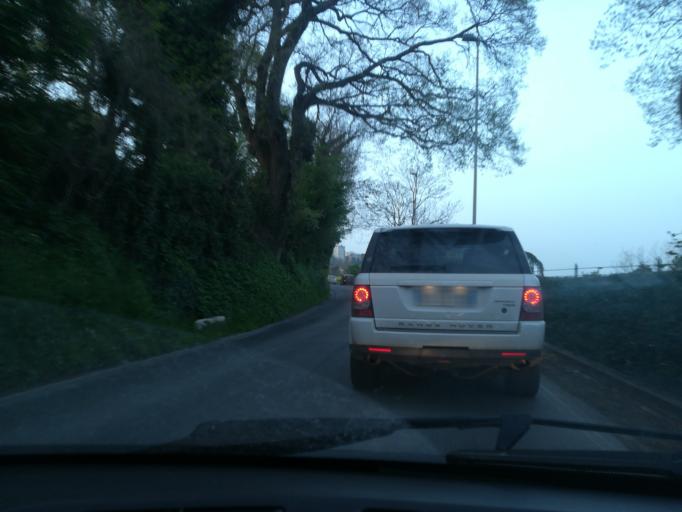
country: IT
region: The Marches
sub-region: Provincia di Macerata
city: Macerata
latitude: 43.2835
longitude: 13.4493
